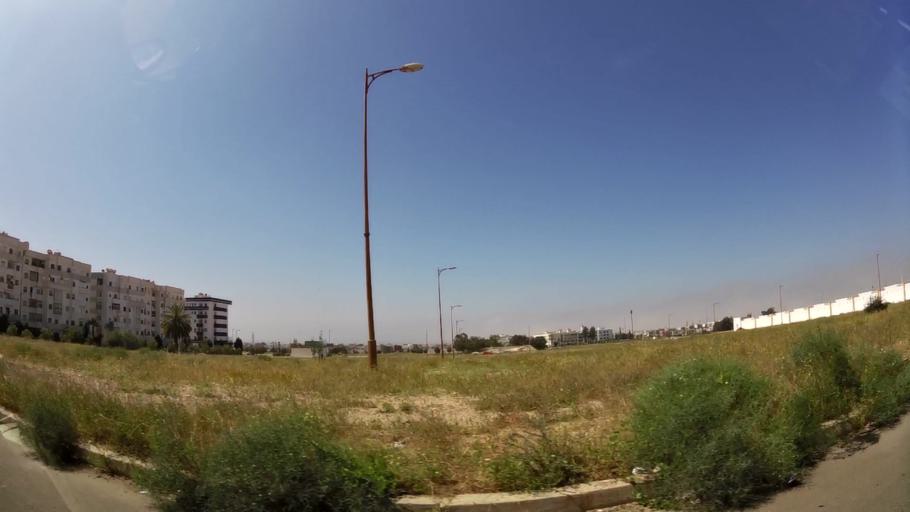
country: MA
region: Oued ed Dahab-Lagouira
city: Dakhla
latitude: 30.4330
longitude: -9.5660
